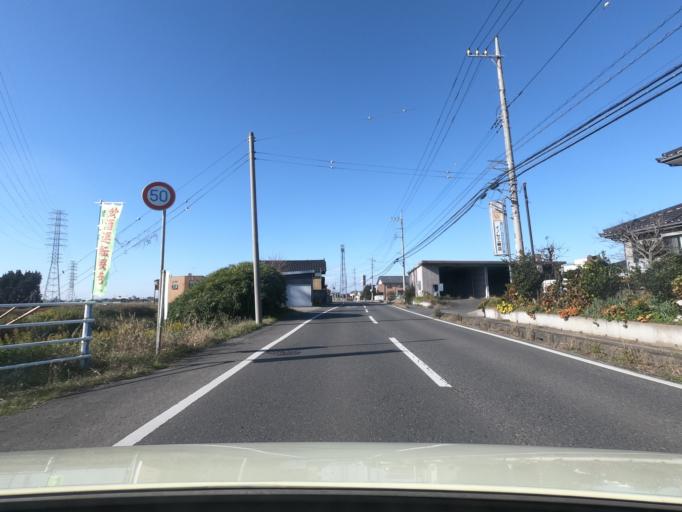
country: JP
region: Ibaraki
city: Ishige
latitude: 36.1743
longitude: 139.9797
